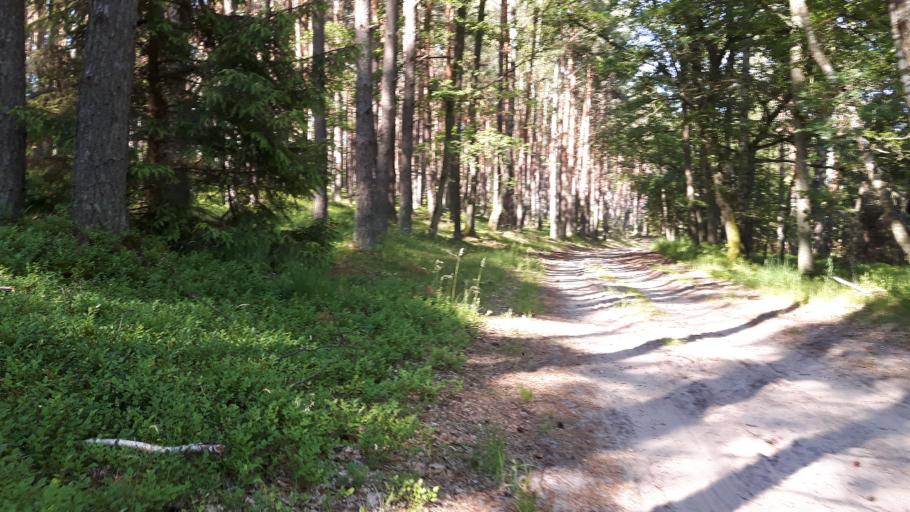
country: PL
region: Pomeranian Voivodeship
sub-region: Powiat leborski
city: Leba
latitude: 54.7024
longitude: 17.5159
